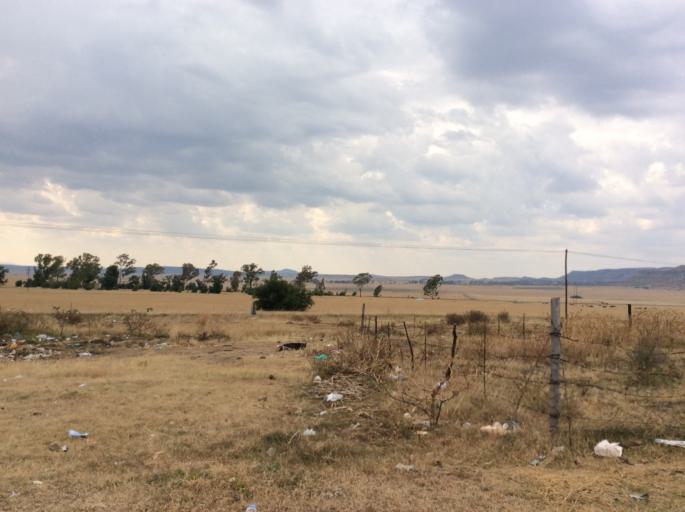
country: ZA
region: Orange Free State
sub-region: Xhariep District Municipality
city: Dewetsdorp
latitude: -29.5750
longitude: 26.6849
